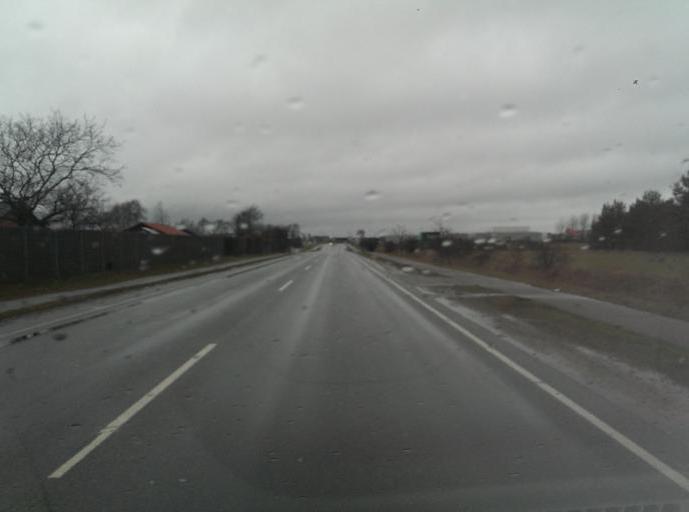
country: DK
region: Central Jutland
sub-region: Ringkobing-Skjern Kommune
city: Skjern
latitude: 55.9476
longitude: 8.5154
